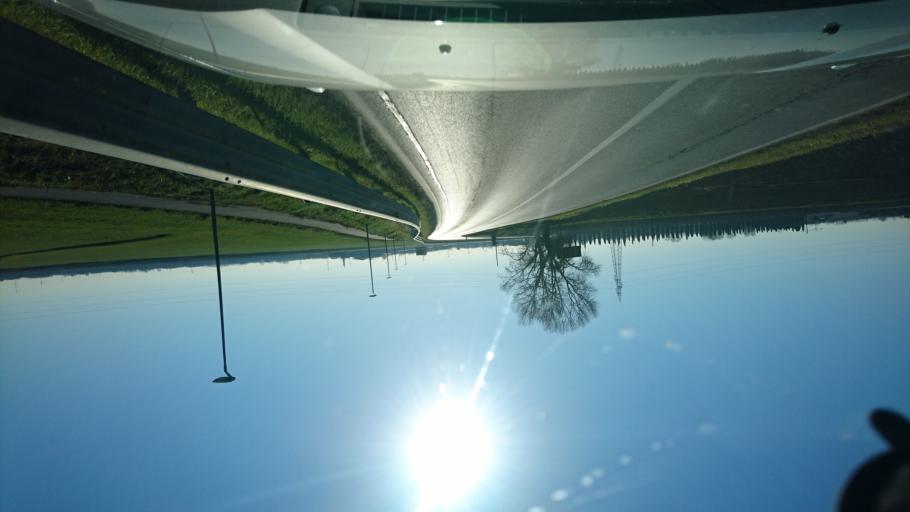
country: IT
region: Veneto
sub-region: Provincia di Rovigo
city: Loreo
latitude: 45.0561
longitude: 12.1996
